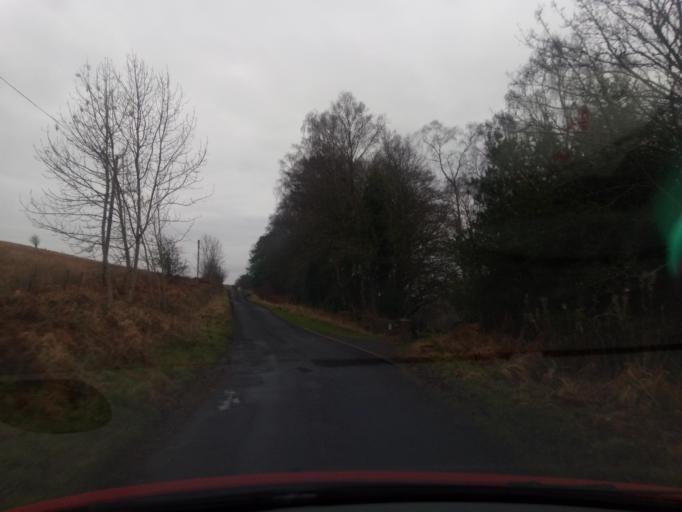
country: GB
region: England
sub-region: Northumberland
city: Rochester
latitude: 55.1766
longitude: -2.4288
